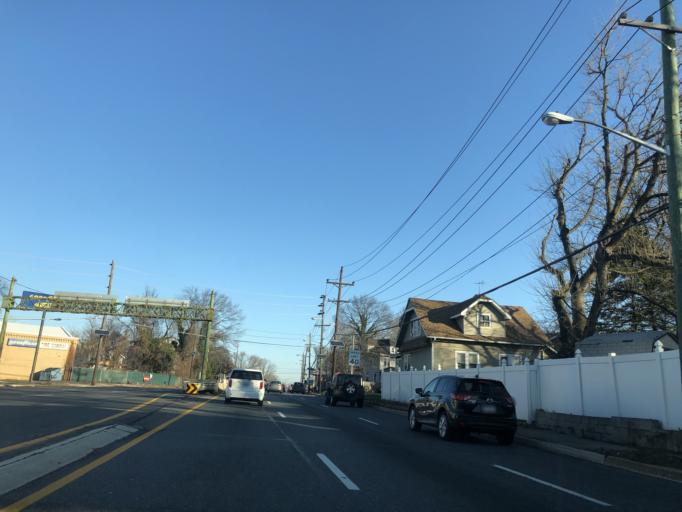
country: US
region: New Jersey
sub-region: Camden County
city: Audubon Park
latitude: 39.9047
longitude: -75.0955
